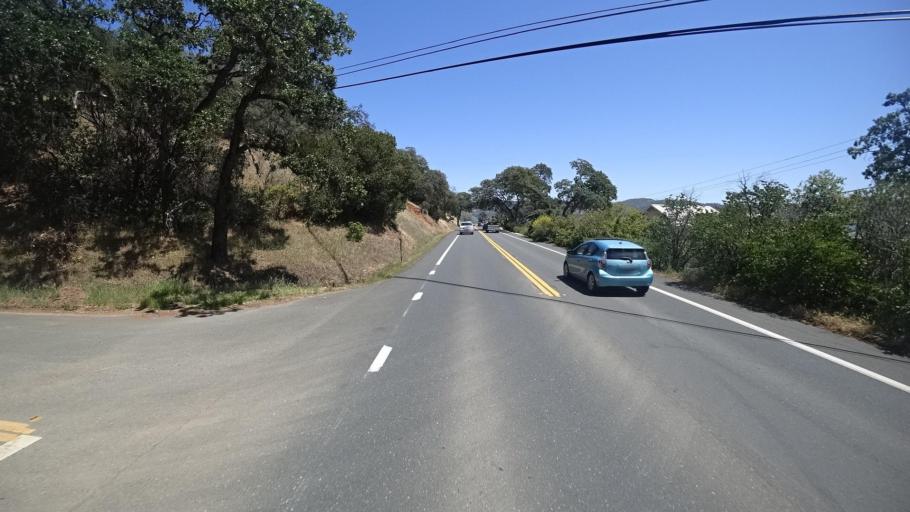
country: US
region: California
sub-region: Lake County
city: Clearlake Oaks
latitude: 39.0208
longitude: -122.7013
